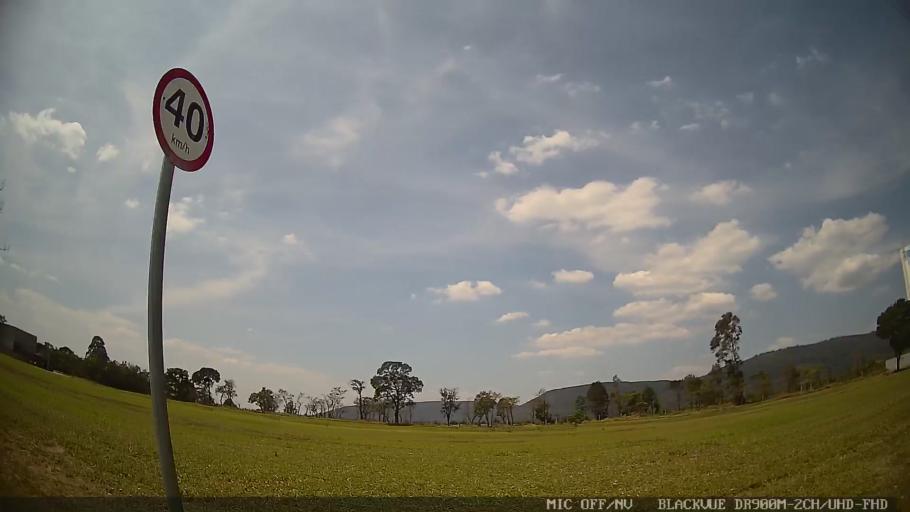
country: BR
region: Sao Paulo
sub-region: Itupeva
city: Itupeva
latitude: -23.2491
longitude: -47.0475
